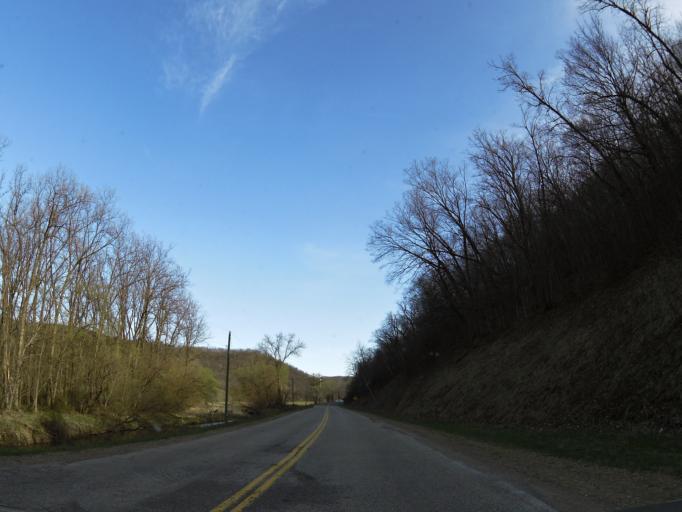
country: US
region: Minnesota
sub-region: Goodhue County
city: Red Wing
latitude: 44.6442
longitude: -92.5880
